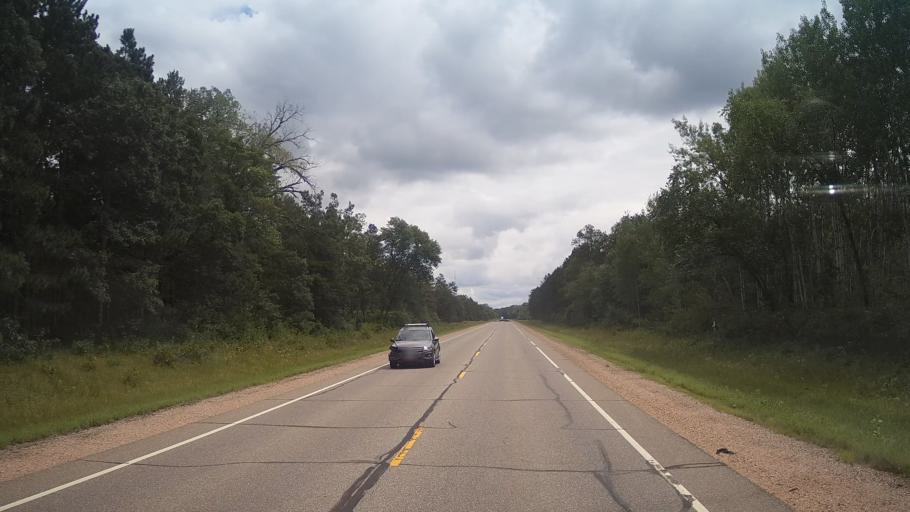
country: US
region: Wisconsin
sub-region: Adams County
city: Friendship
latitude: 44.0475
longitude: -90.0033
